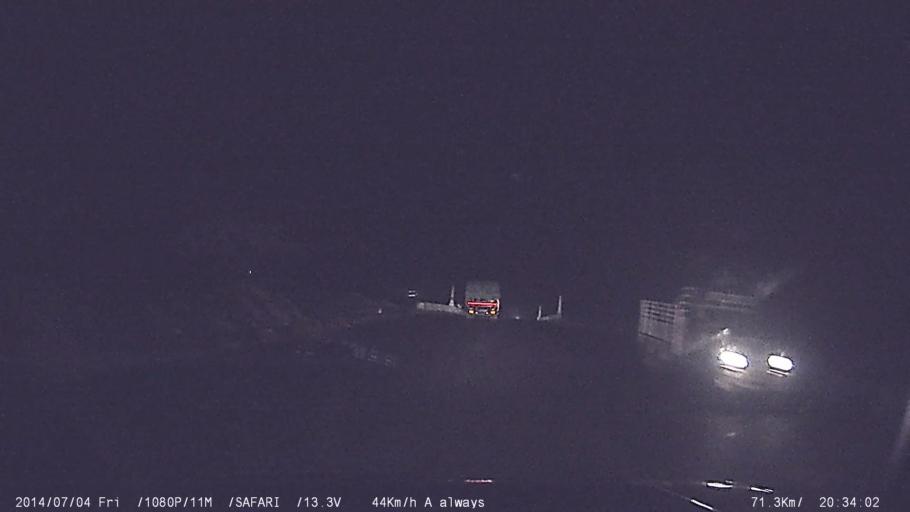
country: IN
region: Tamil Nadu
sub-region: Coimbatore
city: Madukkarai
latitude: 10.9276
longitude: 76.9495
